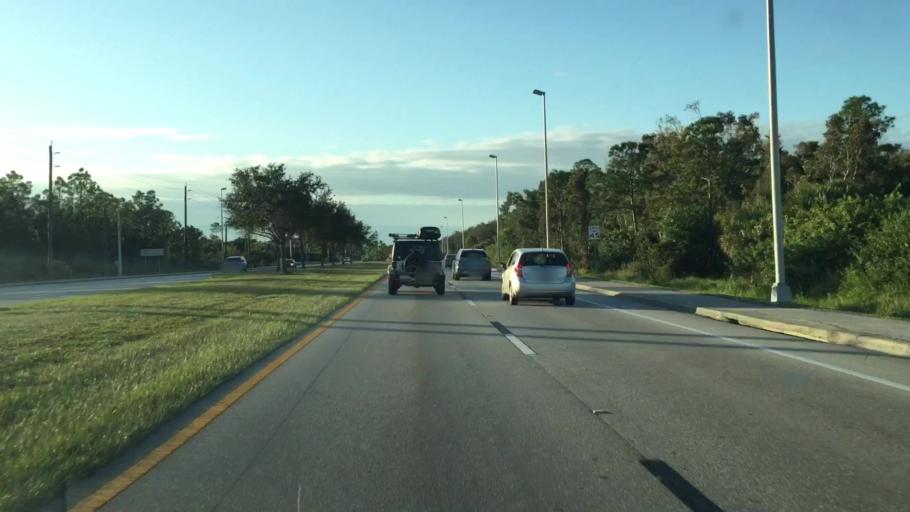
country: US
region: Florida
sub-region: Lee County
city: Estero
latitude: 26.4483
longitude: -81.7890
